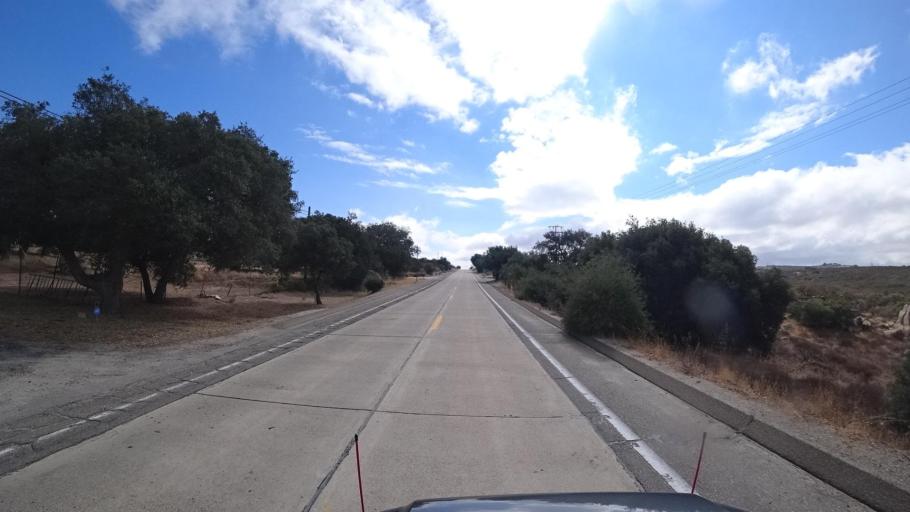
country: US
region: California
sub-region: San Diego County
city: Campo
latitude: 32.6726
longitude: -116.3213
